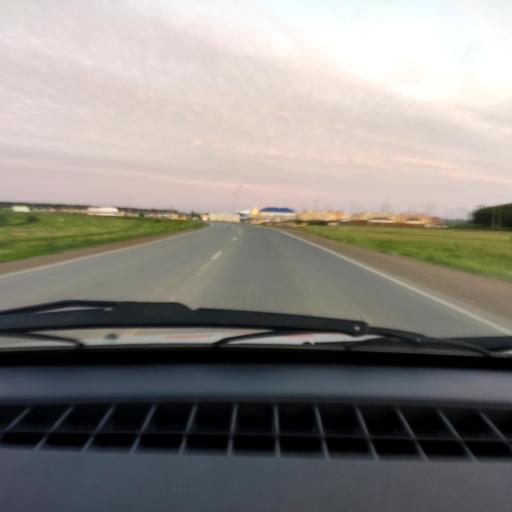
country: RU
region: Bashkortostan
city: Ufa
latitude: 54.6283
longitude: 55.8968
